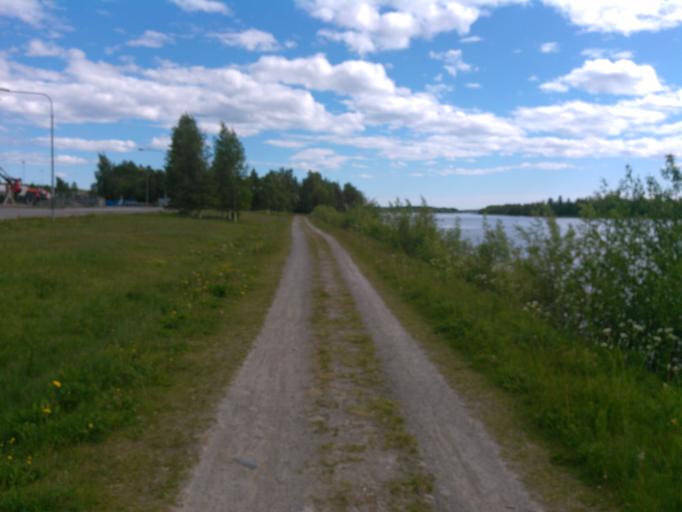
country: SE
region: Vaesterbotten
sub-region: Umea Kommun
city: Umea
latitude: 63.7953
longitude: 20.3030
